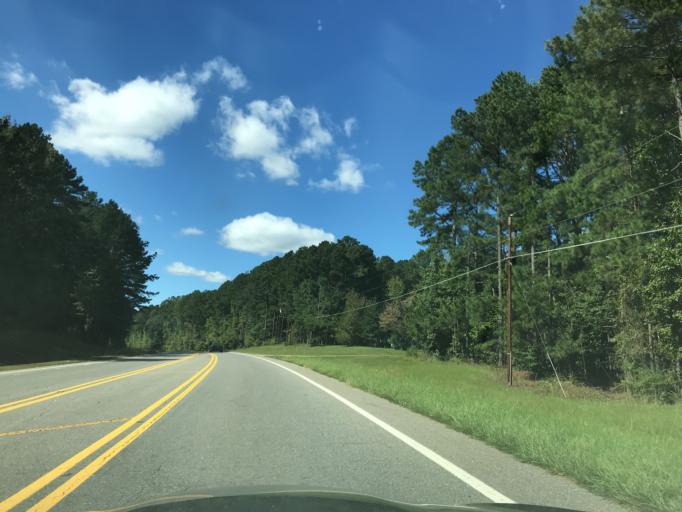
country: US
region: North Carolina
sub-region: Granville County
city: Creedmoor
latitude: 35.9891
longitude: -78.6967
